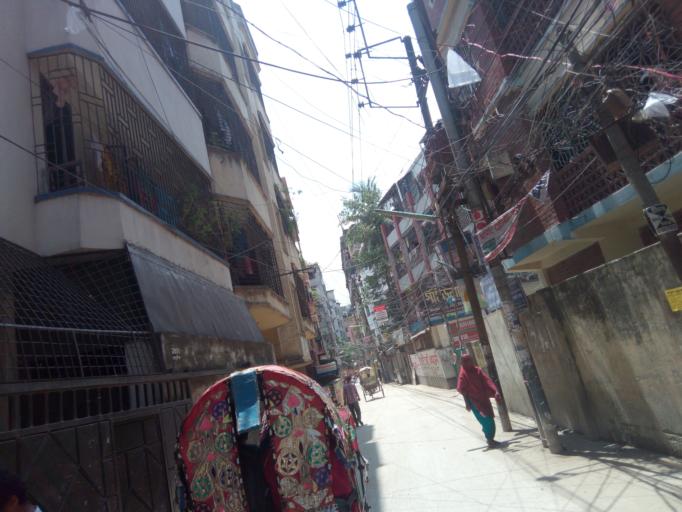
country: BD
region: Dhaka
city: Azimpur
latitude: 23.7628
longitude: 90.3927
